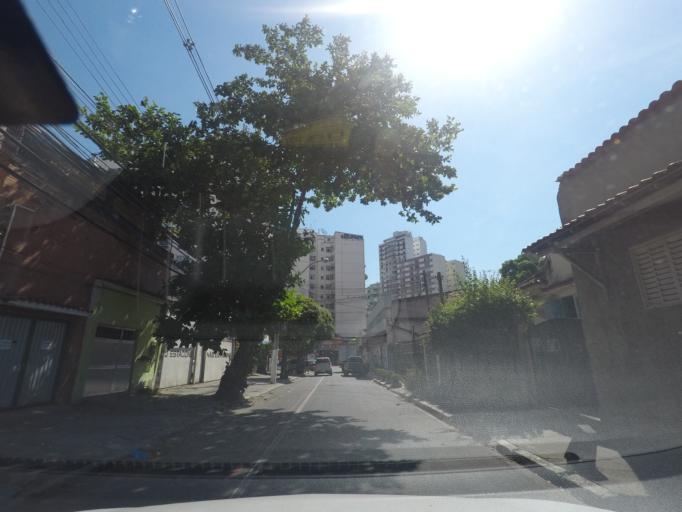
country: BR
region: Rio de Janeiro
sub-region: Niteroi
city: Niteroi
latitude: -22.8998
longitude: -43.1114
